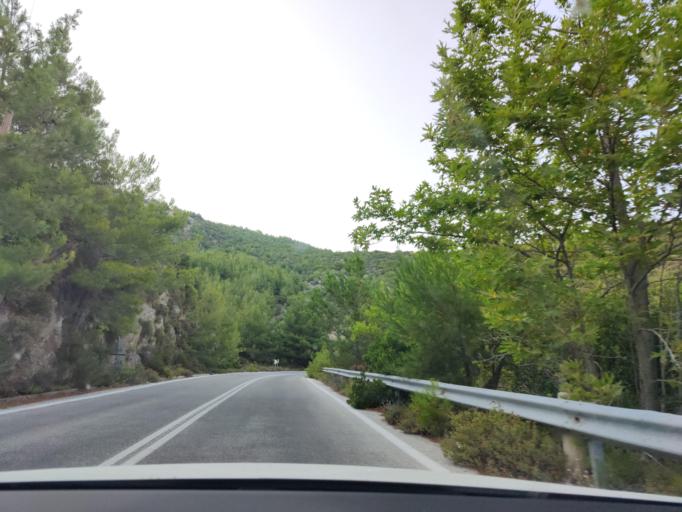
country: GR
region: East Macedonia and Thrace
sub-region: Nomos Kavalas
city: Potamia
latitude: 40.6209
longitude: 24.7591
